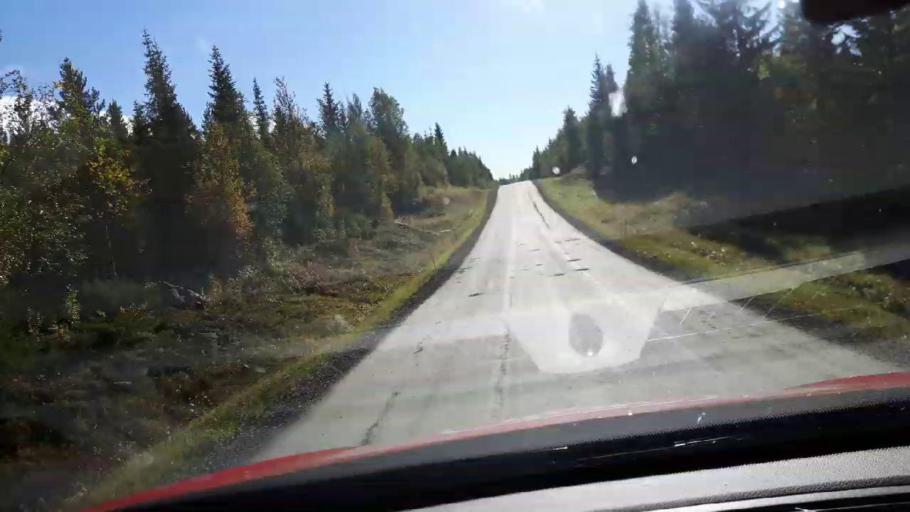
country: NO
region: Nord-Trondelag
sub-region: Lierne
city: Sandvika
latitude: 64.6016
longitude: 13.9700
